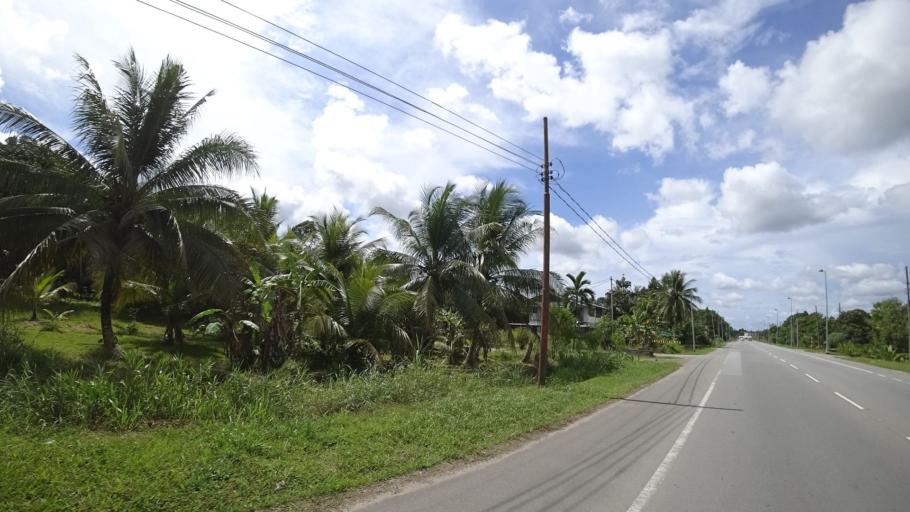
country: BN
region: Tutong
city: Tutong
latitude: 4.7549
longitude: 114.8192
